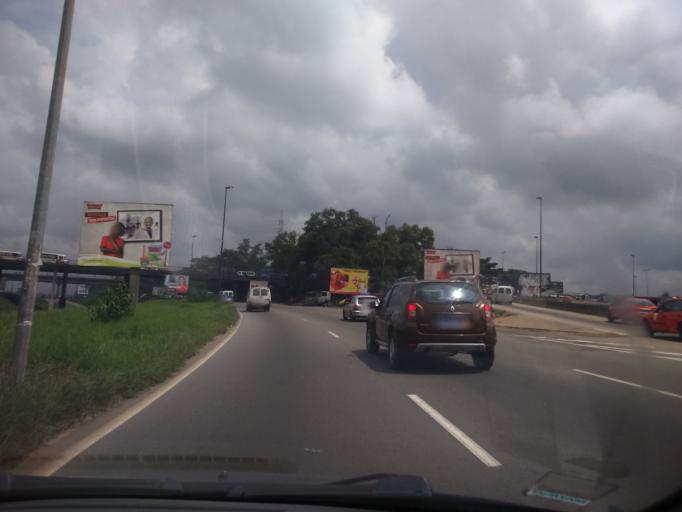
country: CI
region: Lagunes
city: Abobo
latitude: 5.3650
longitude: -4.0281
